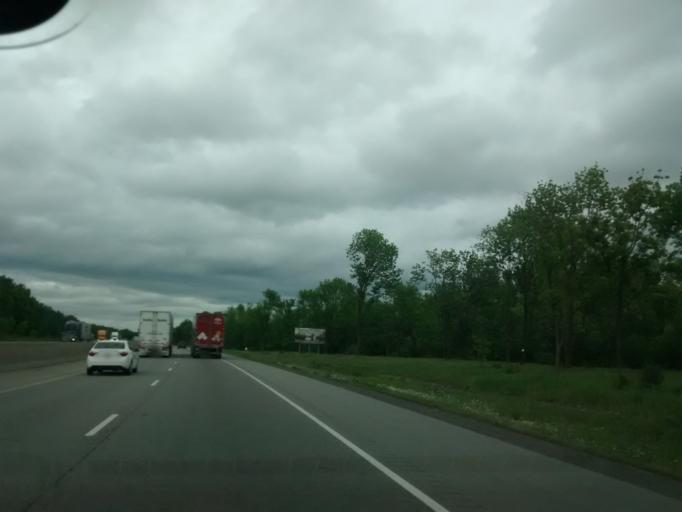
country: CA
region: Ontario
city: Brockville
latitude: 44.6334
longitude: -75.6502
